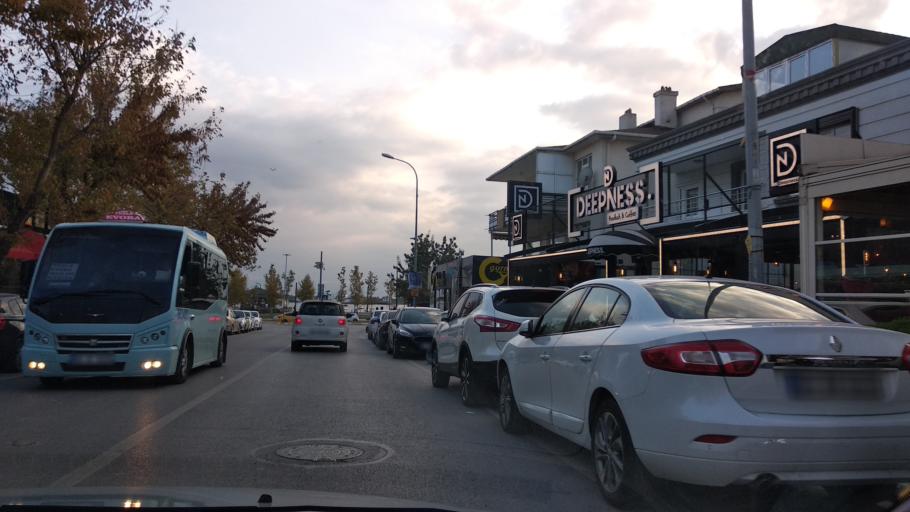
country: TR
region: Istanbul
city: Icmeler
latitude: 40.8176
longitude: 29.2982
